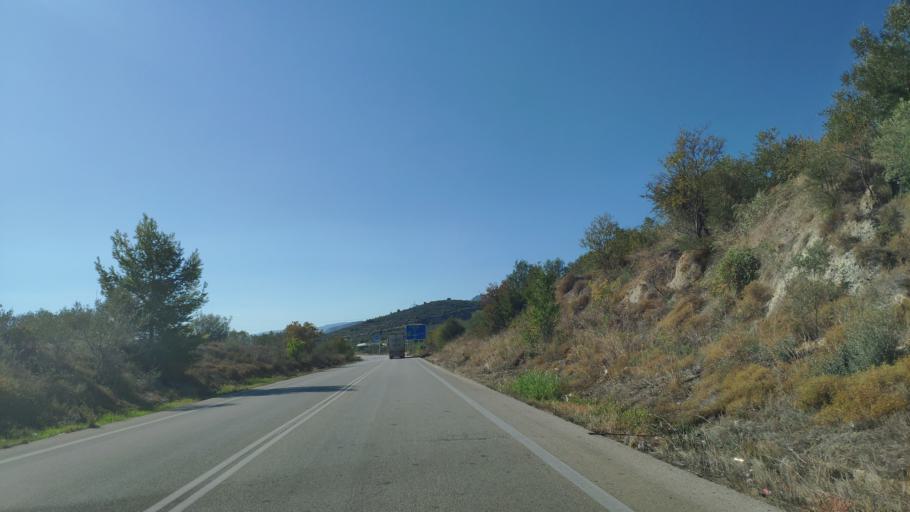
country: GR
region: Peloponnese
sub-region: Nomos Korinthias
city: Arkhaia Korinthos
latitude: 37.9019
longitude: 22.8970
